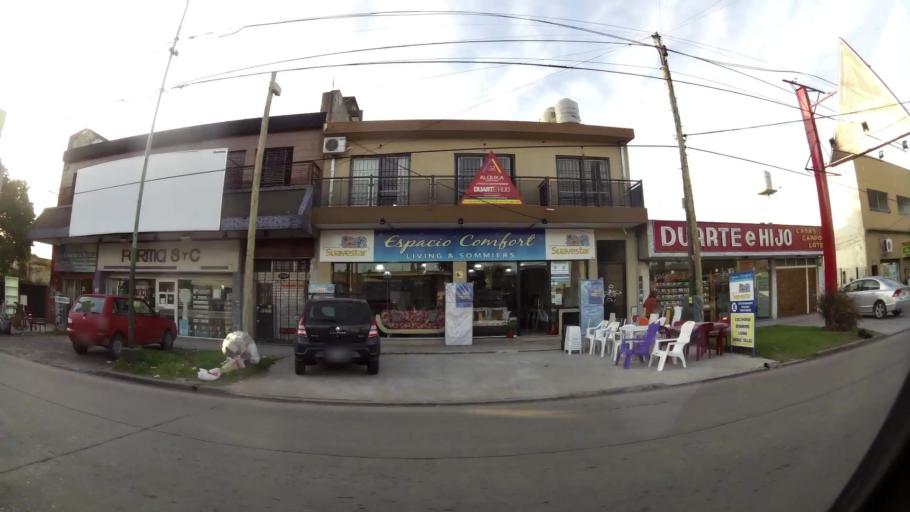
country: AR
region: Buenos Aires
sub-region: Partido de Almirante Brown
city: Adrogue
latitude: -34.7933
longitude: -58.3600
